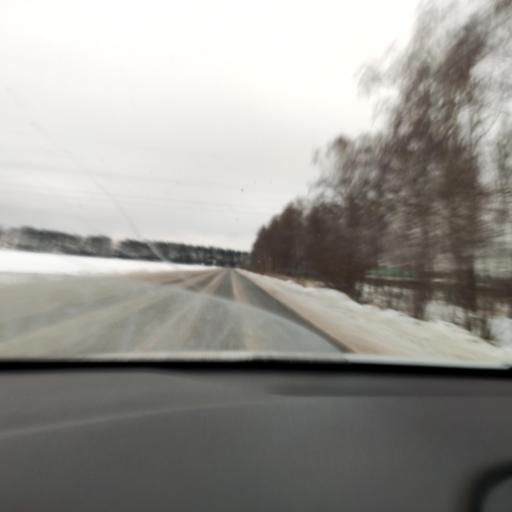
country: RU
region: Tatarstan
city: Osinovo
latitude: 55.8893
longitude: 48.8907
